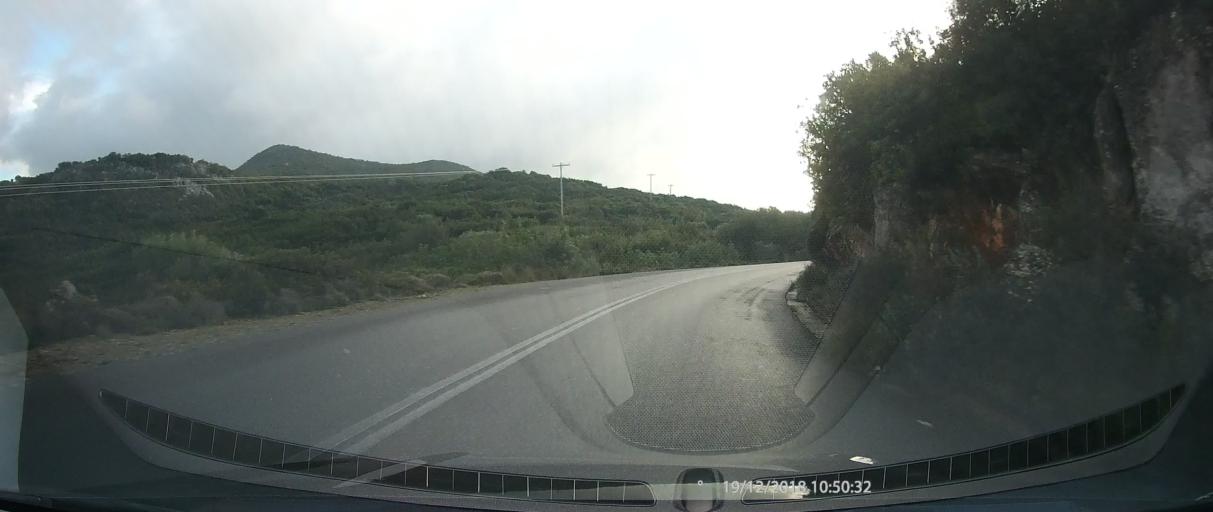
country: GR
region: Peloponnese
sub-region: Nomos Messinias
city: Kardamyli
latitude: 36.9238
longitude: 22.2082
